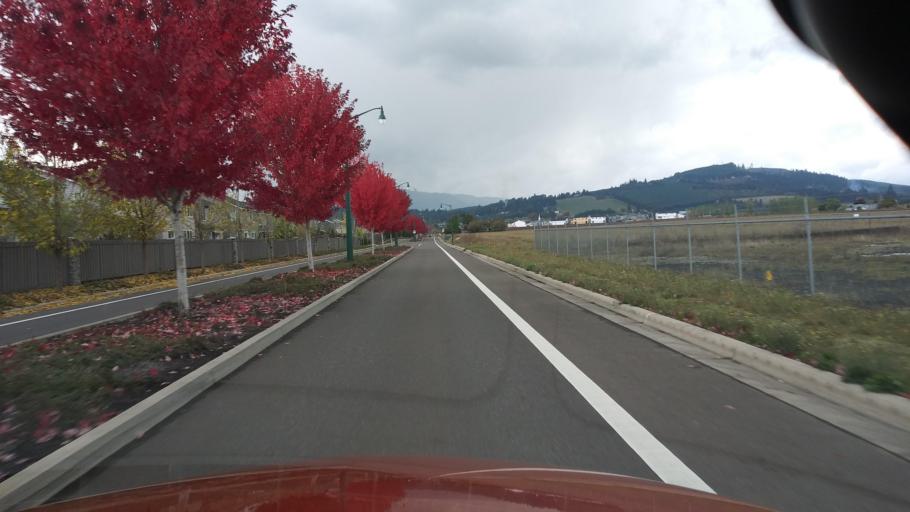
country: US
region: Oregon
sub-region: Washington County
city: Forest Grove
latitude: 45.5391
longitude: -123.1092
